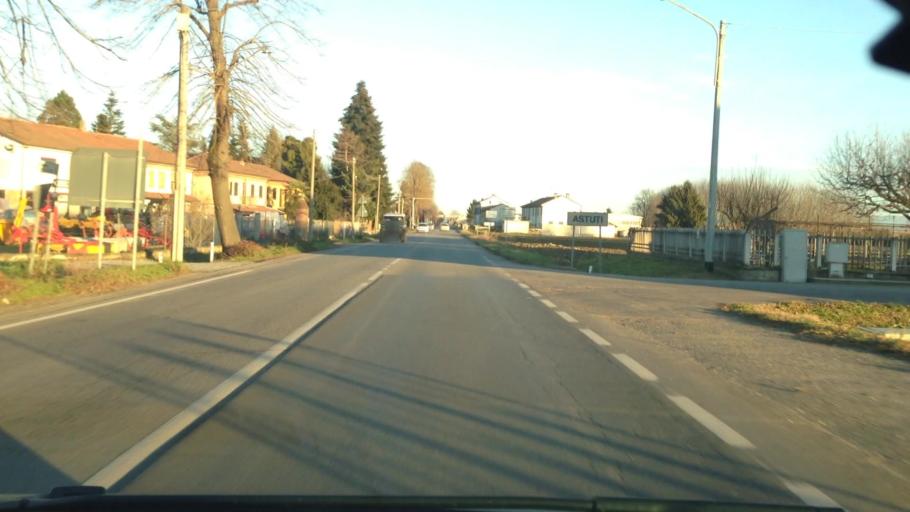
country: IT
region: Piedmont
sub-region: Provincia di Alessandria
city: Alessandria
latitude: 44.9216
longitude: 8.5629
